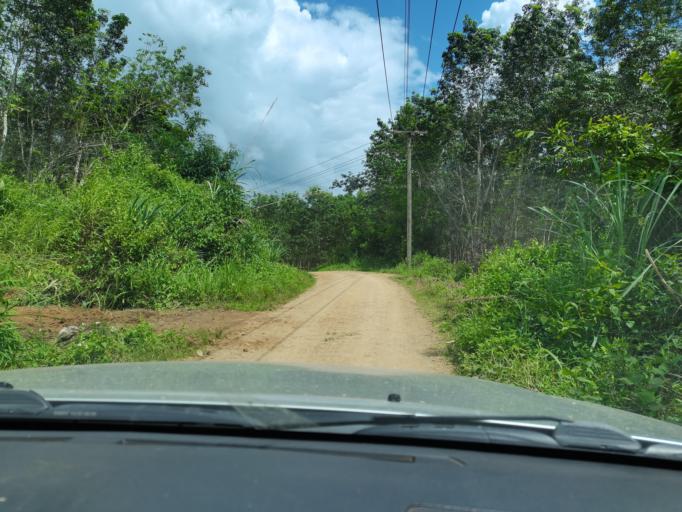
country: LA
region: Loungnamtha
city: Muang Long
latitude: 20.6858
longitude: 101.0443
